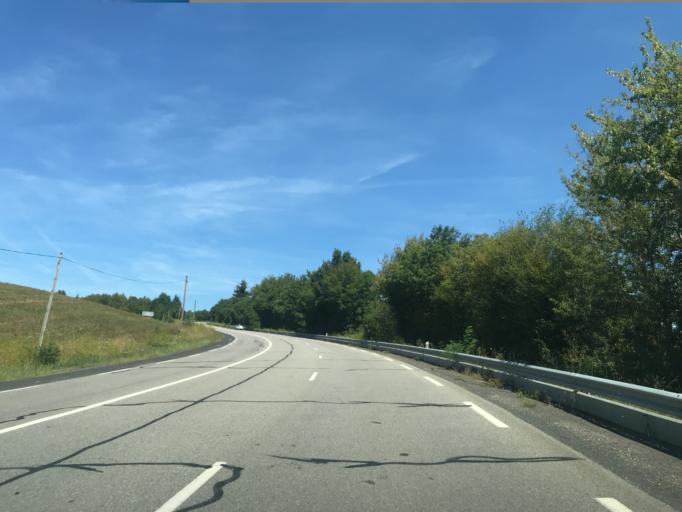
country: FR
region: Limousin
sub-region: Departement de la Correze
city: Naves
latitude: 45.2981
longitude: 1.8150
